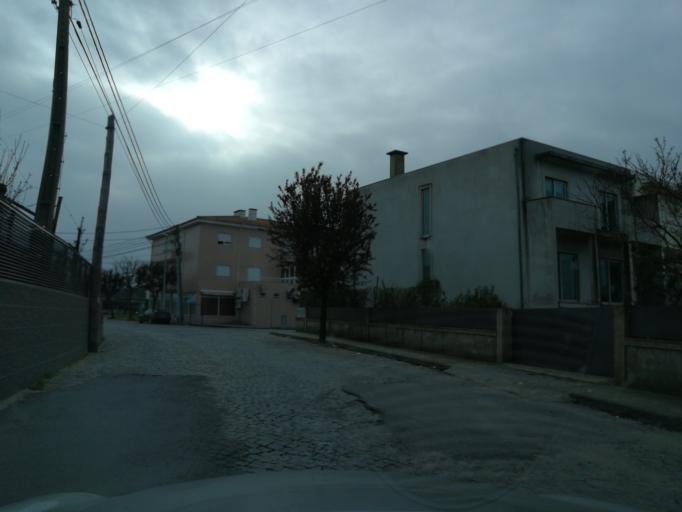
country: PT
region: Braga
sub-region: Braga
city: Adaufe
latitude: 41.5824
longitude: -8.4293
